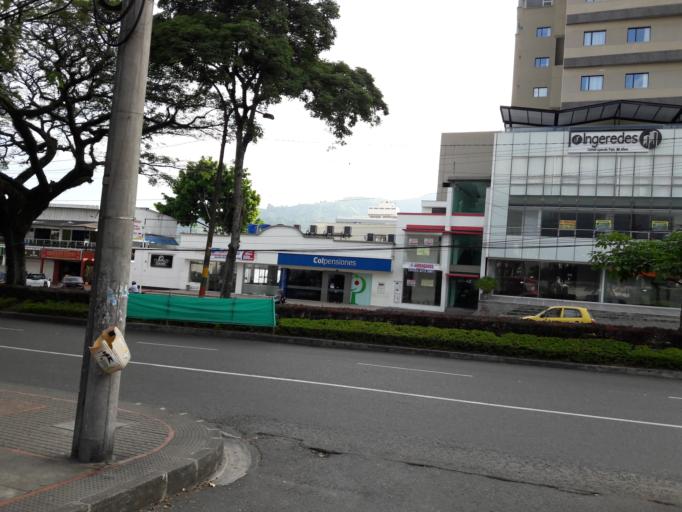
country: CO
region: Tolima
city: Ibague
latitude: 4.4361
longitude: -75.2129
